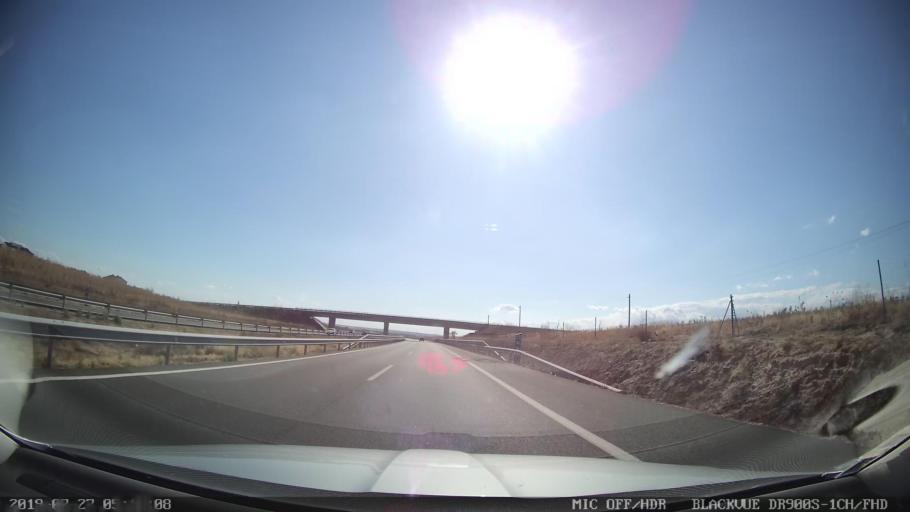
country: ES
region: Castille-La Mancha
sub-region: Province of Toledo
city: Santa Olalla
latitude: 40.0349
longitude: -4.4272
